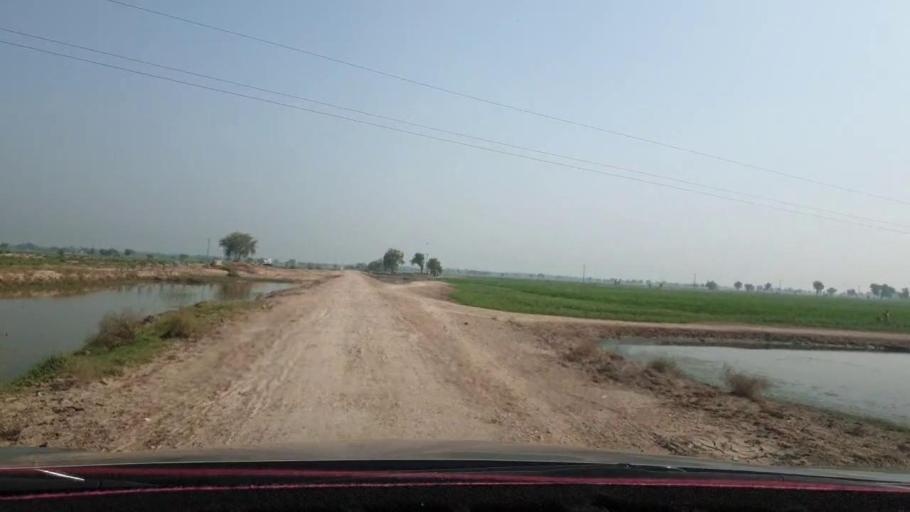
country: PK
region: Sindh
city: Kambar
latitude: 27.4956
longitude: 67.9302
